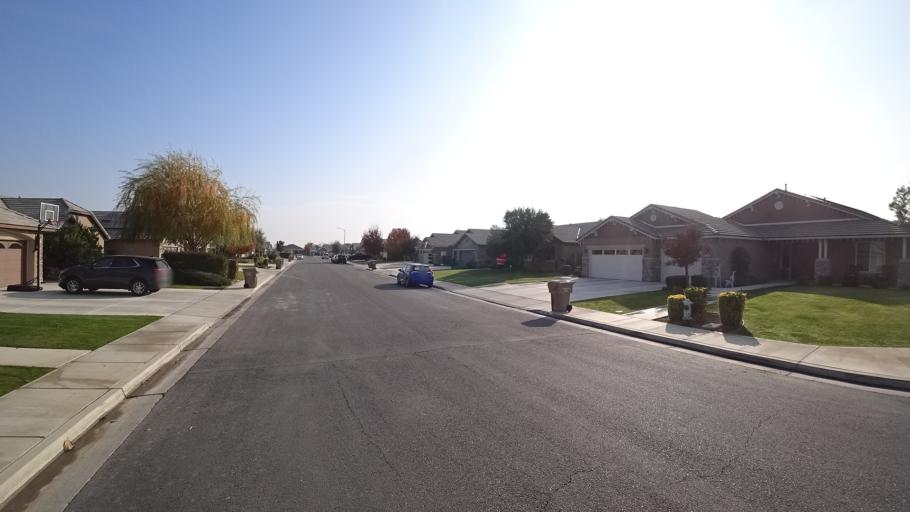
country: US
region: California
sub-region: Kern County
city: Greenacres
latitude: 35.4345
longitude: -119.1217
